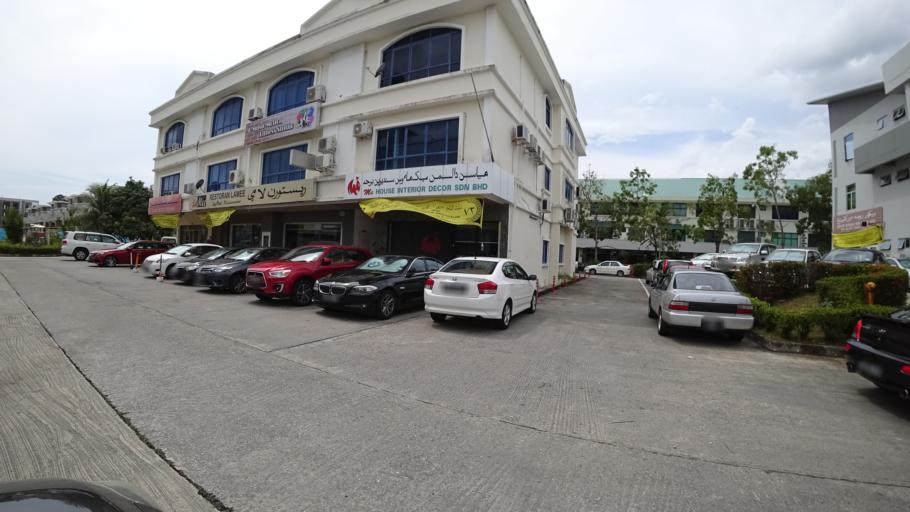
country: BN
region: Brunei and Muara
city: Bandar Seri Begawan
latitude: 4.8951
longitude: 114.9204
